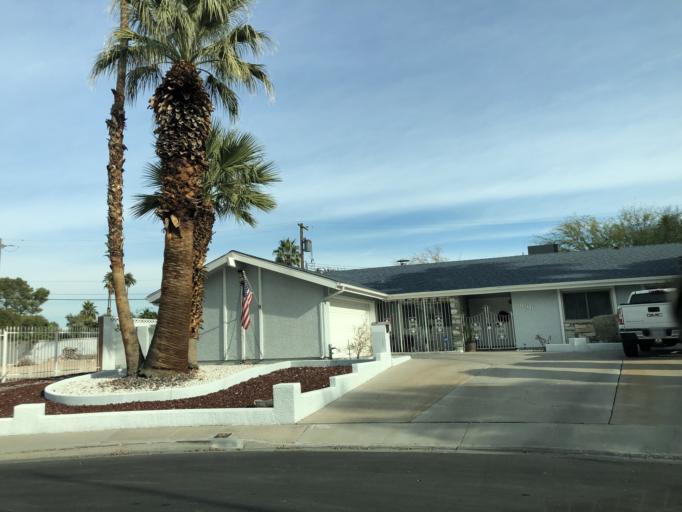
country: US
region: Nevada
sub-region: Clark County
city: Winchester
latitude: 36.1193
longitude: -115.1228
